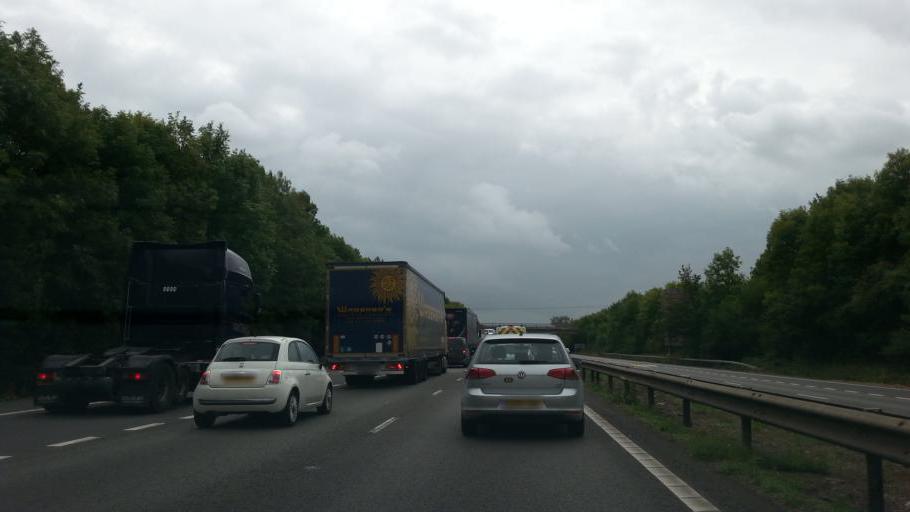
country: GB
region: England
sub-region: Cambridgeshire
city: Girton
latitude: 52.2109
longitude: 0.0775
